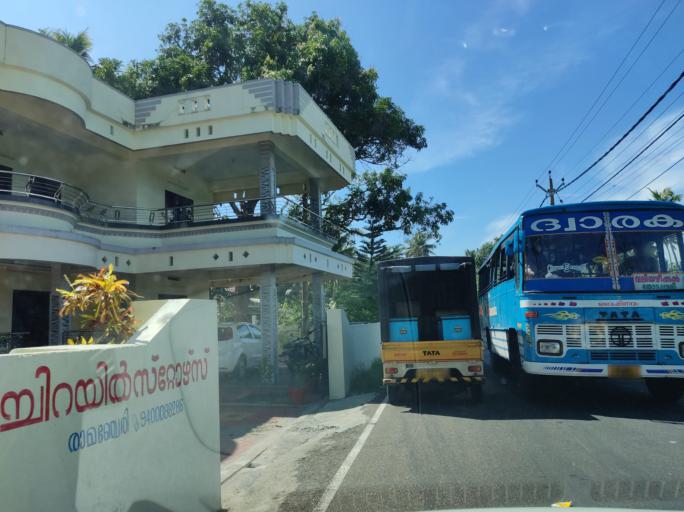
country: IN
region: Kerala
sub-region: Alappuzha
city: Kayankulam
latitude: 9.1753
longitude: 76.4457
